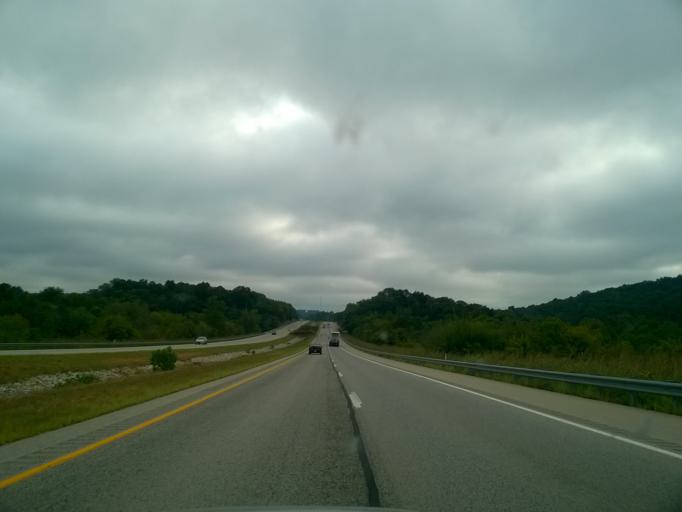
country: US
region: Indiana
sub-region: Harrison County
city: Corydon
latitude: 38.2353
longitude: -86.2292
